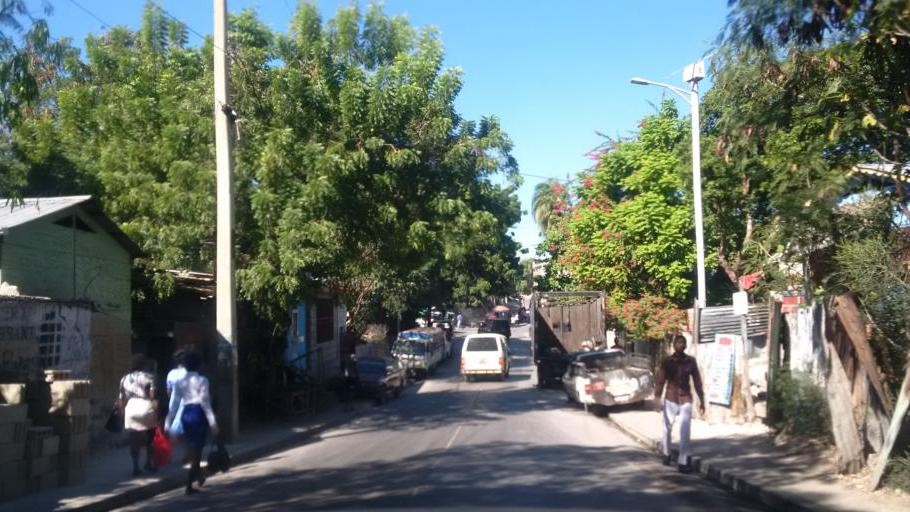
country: HT
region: Ouest
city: Port-au-Prince
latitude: 18.5452
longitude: -72.3213
